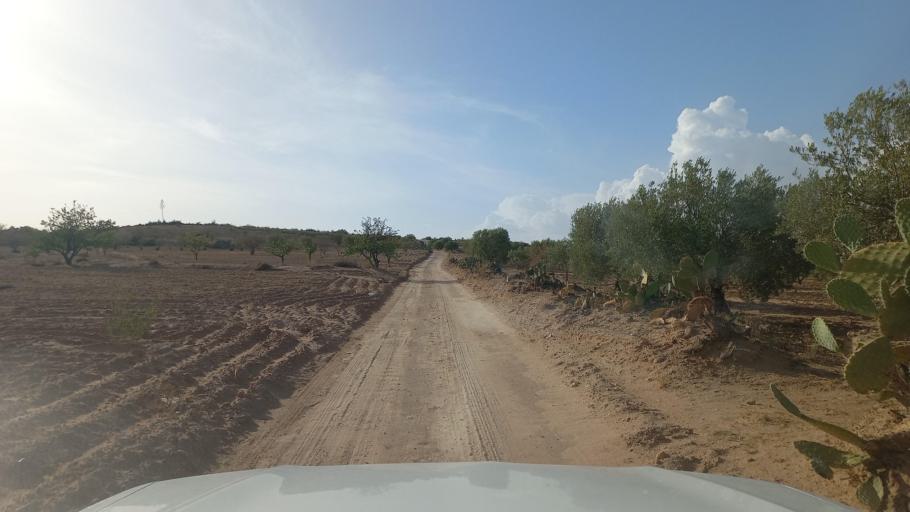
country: TN
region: Al Qasrayn
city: Kasserine
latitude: 35.2335
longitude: 8.9199
